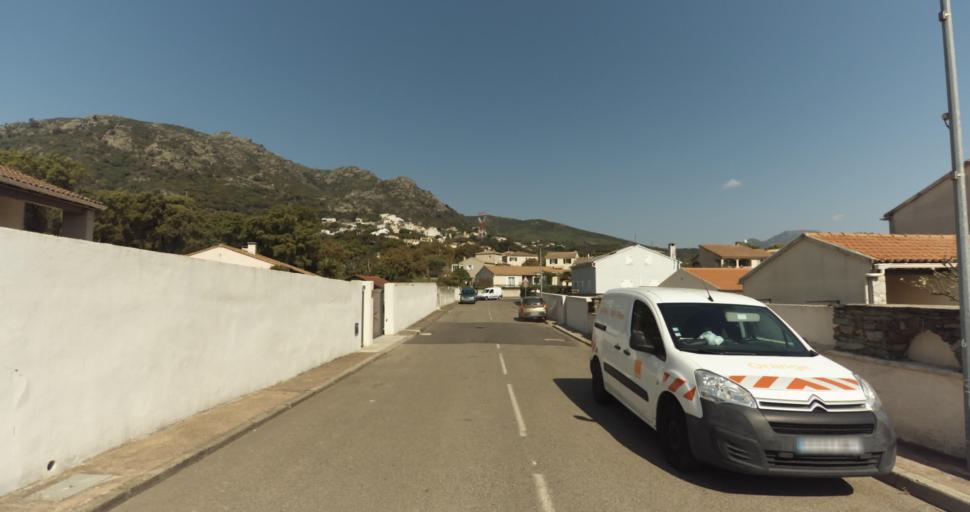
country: FR
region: Corsica
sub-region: Departement de la Haute-Corse
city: Biguglia
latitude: 42.6239
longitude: 9.4279
